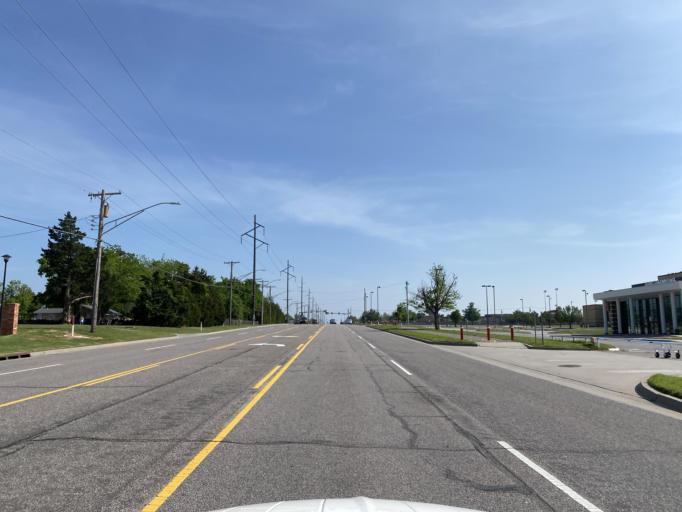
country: US
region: Oklahoma
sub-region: Oklahoma County
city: Midwest City
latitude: 35.4445
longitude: -97.3532
